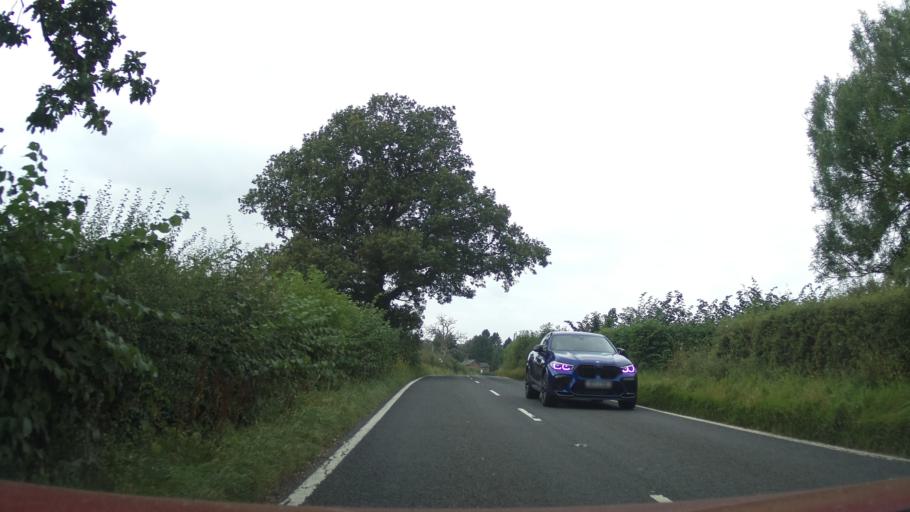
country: GB
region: England
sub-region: Derbyshire
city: Wirksworth
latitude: 53.0265
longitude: -1.5602
